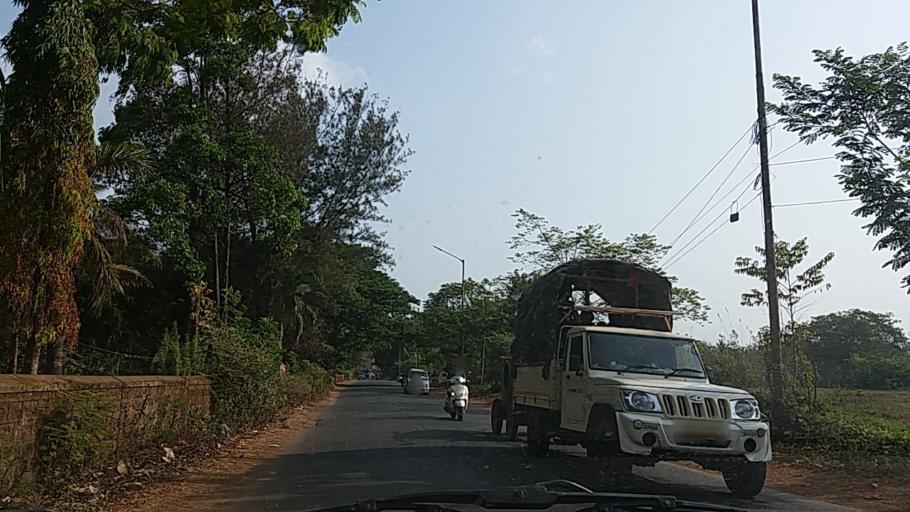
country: IN
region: Goa
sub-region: South Goa
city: Madgaon
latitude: 15.2636
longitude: 73.9701
